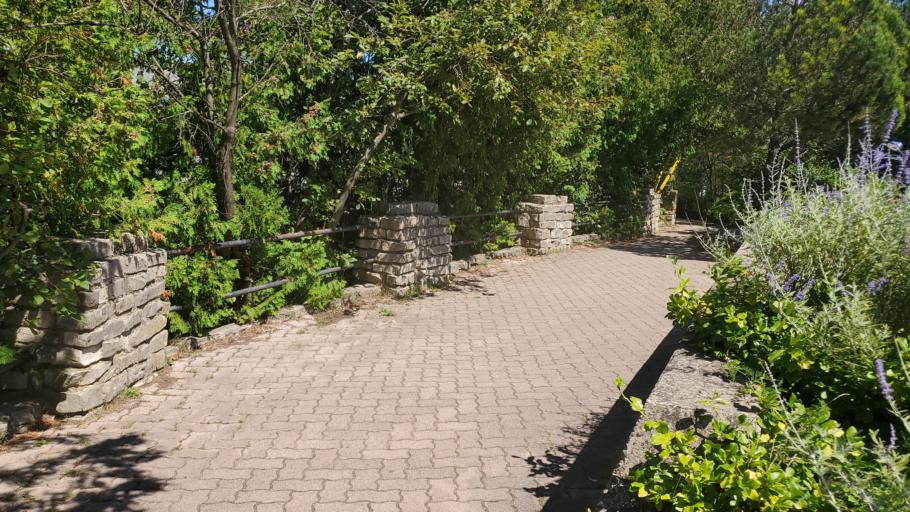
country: CA
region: Ontario
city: Tobermory
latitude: 45.2568
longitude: -81.6619
